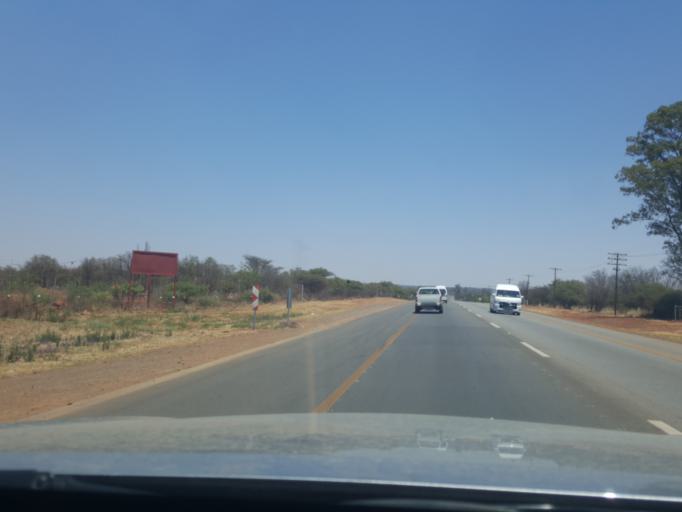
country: ZA
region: North-West
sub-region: Ngaka Modiri Molema District Municipality
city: Zeerust
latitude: -25.5560
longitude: 26.0678
